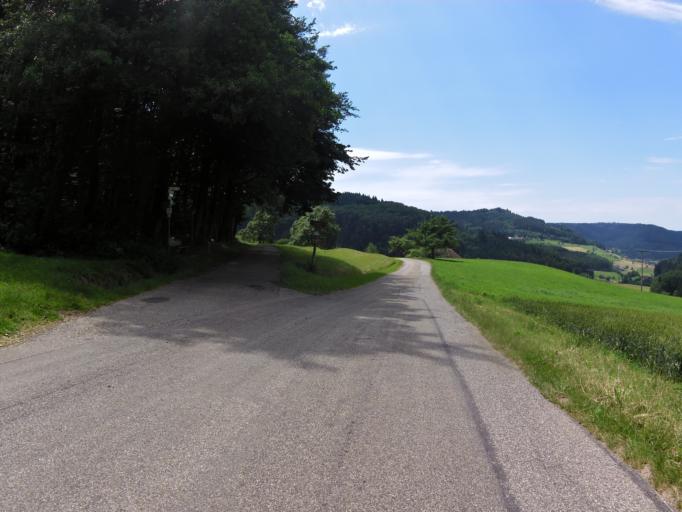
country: DE
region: Baden-Wuerttemberg
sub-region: Freiburg Region
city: Seelbach
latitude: 48.3258
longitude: 7.9786
